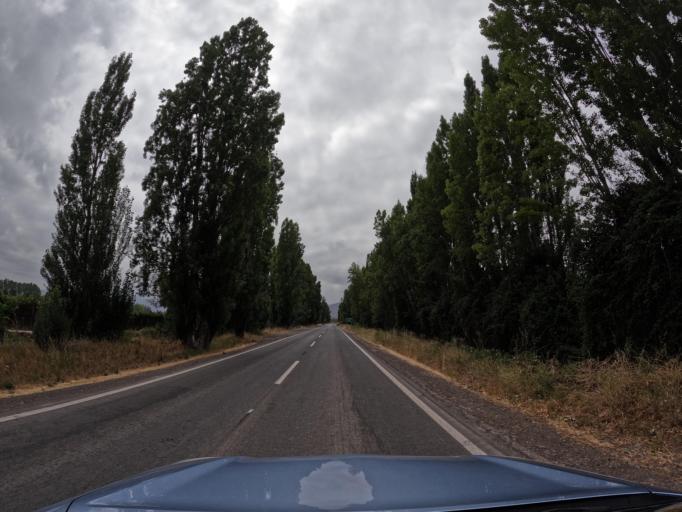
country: CL
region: Maule
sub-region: Provincia de Curico
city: Teno
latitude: -34.7517
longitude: -71.2226
